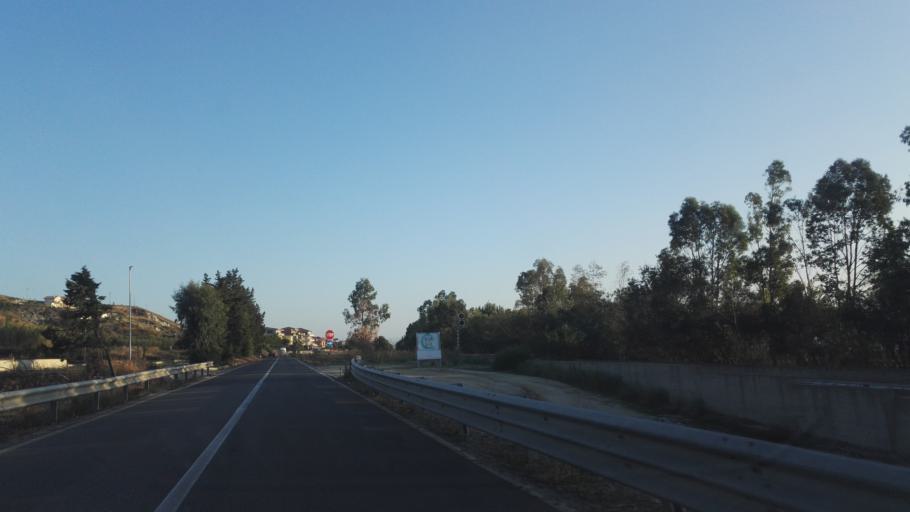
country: IT
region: Calabria
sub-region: Provincia di Catanzaro
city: Santa Caterina dello Ionio Marina
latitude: 38.5128
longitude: 16.5735
